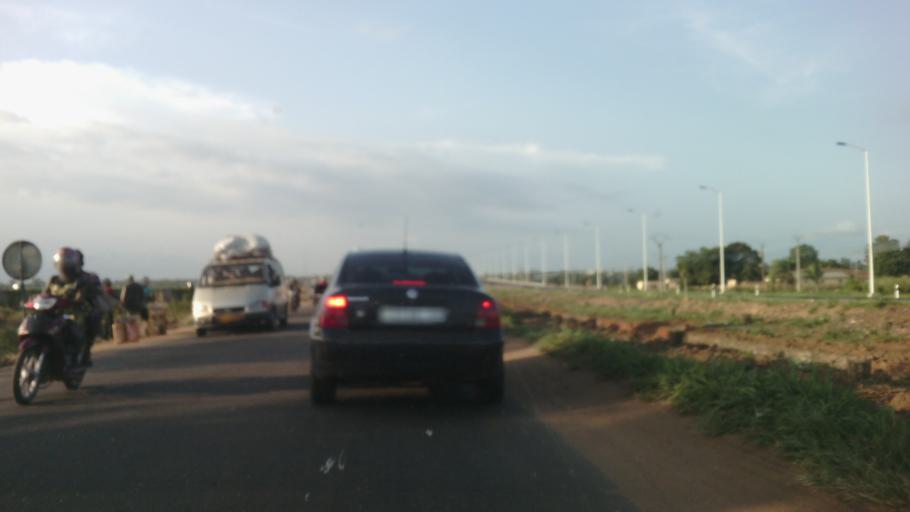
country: TG
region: Maritime
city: Tsevie
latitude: 6.3016
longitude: 1.2144
